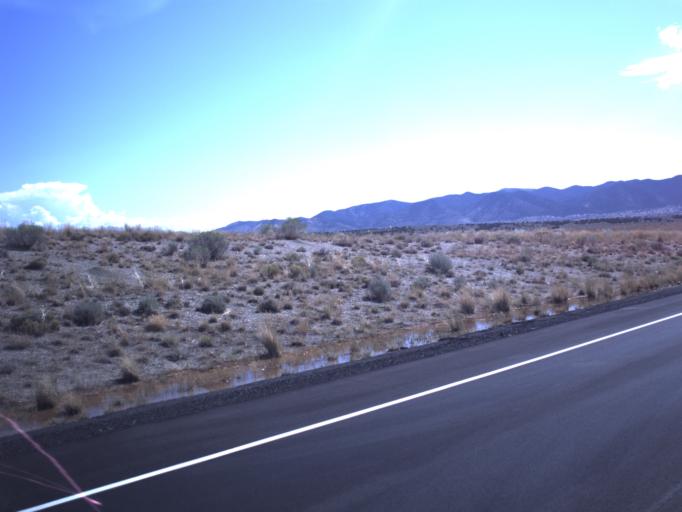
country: US
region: Utah
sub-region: Utah County
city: Eagle Mountain
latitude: 40.0644
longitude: -112.3198
